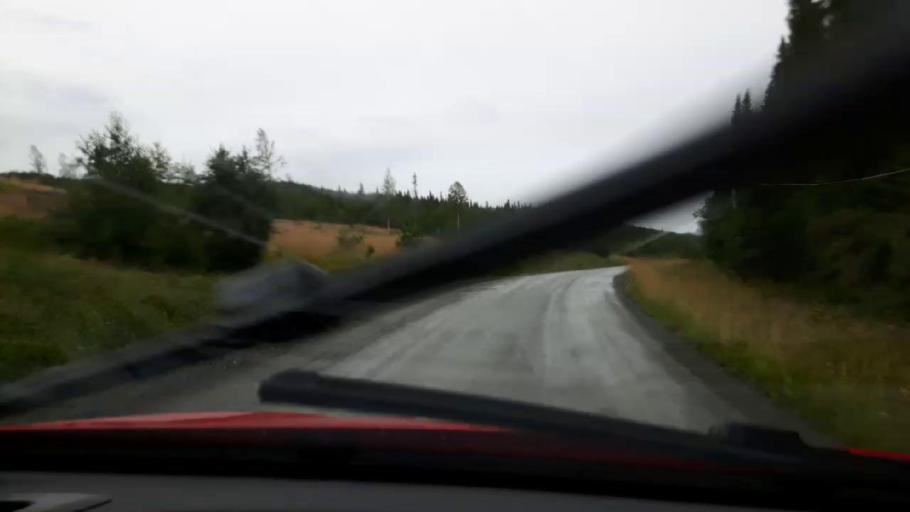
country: SE
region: Jaemtland
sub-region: Are Kommun
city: Are
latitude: 63.4250
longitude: 12.8172
